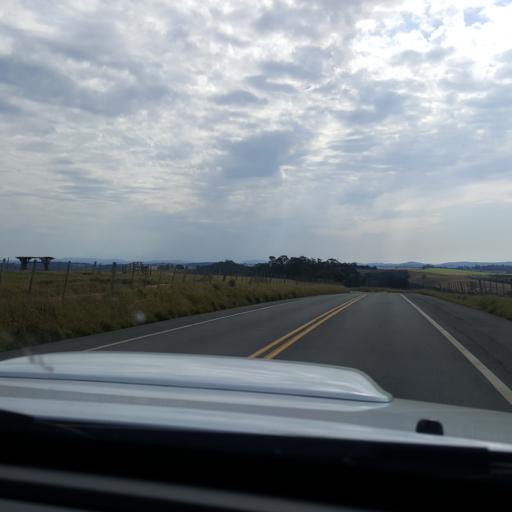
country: BR
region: Sao Paulo
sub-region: Itaporanga
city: Itaporanga
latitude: -23.7766
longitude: -49.4317
